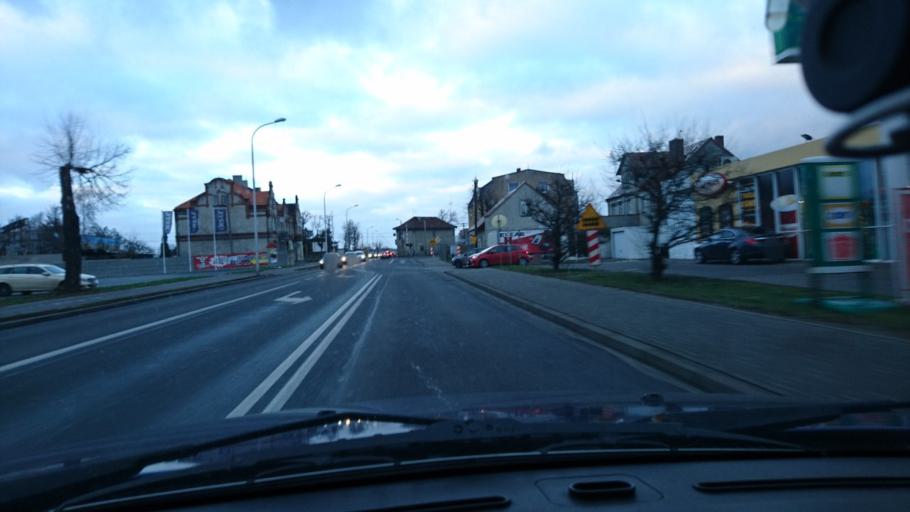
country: PL
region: Greater Poland Voivodeship
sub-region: Powiat kepinski
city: Kepno
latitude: 51.2888
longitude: 17.9935
